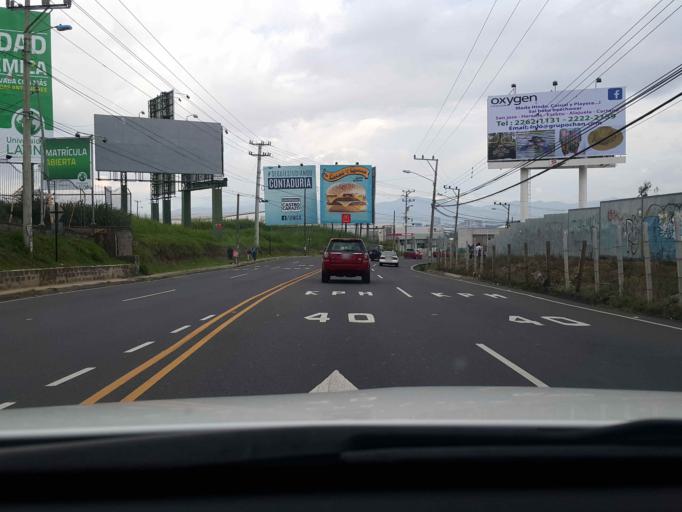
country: CR
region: Heredia
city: San Pablo
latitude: 9.9847
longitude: -84.1093
